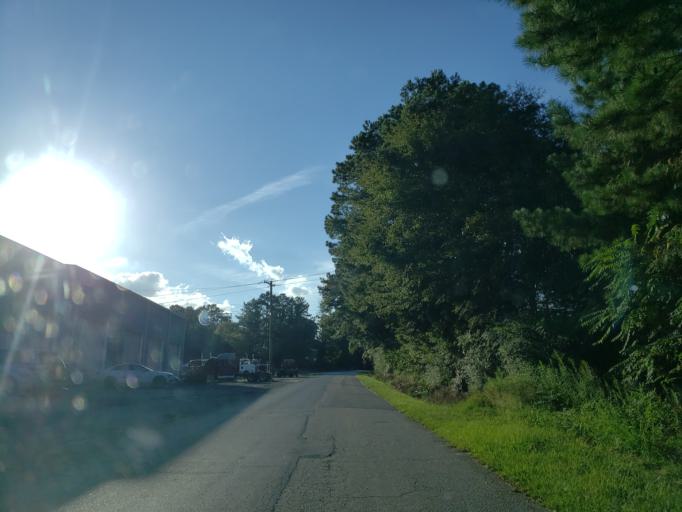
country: US
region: Georgia
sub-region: Bartow County
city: Cartersville
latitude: 34.2114
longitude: -84.8336
